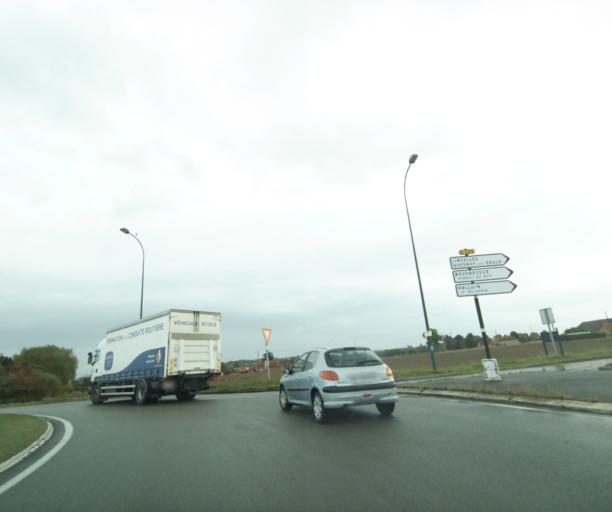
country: FR
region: Nord-Pas-de-Calais
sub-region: Departement du Nord
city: Bousbecque
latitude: 50.7700
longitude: 3.1050
